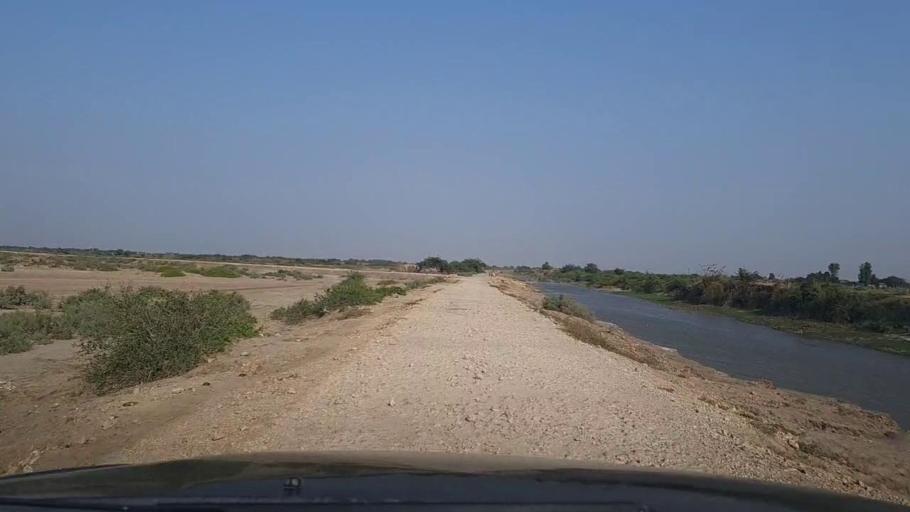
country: PK
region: Sindh
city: Mirpur Sakro
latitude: 24.6414
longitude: 67.7503
